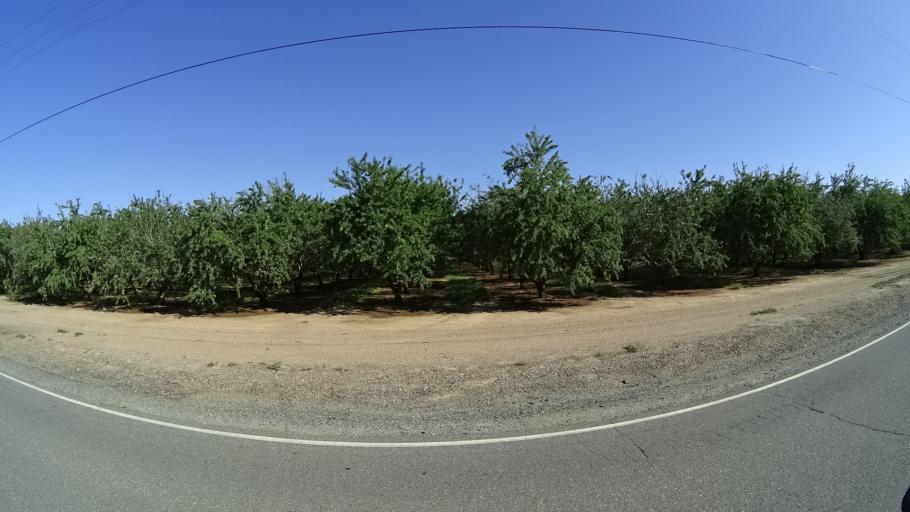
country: US
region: California
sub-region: Glenn County
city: Hamilton City
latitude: 39.7091
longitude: -122.0468
